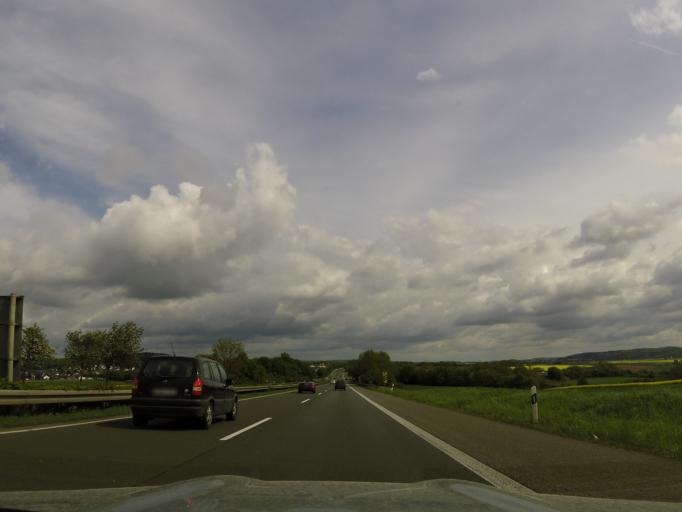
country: DE
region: Hesse
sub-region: Regierungsbezirk Giessen
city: Dehrn
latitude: 50.4261
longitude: 8.0868
